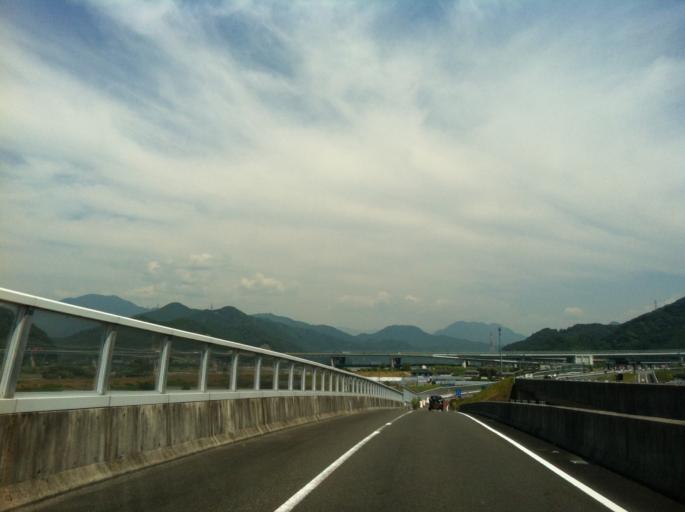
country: JP
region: Shizuoka
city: Shizuoka-shi
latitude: 35.0334
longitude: 138.3782
